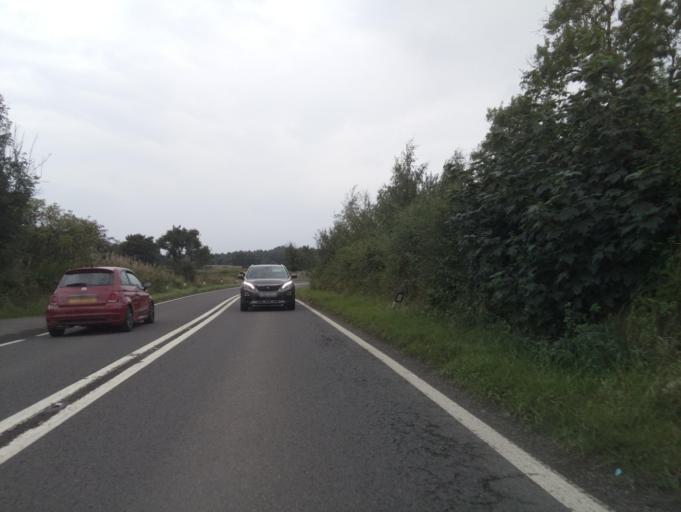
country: GB
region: Scotland
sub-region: Dumfries and Galloway
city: Locharbriggs
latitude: 55.1161
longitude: -3.5753
